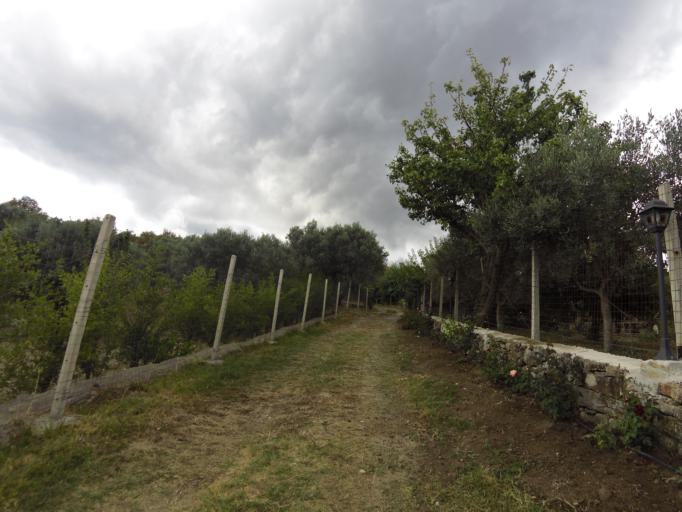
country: IT
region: Calabria
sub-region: Provincia di Reggio Calabria
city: Camini
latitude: 38.4449
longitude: 16.4554
